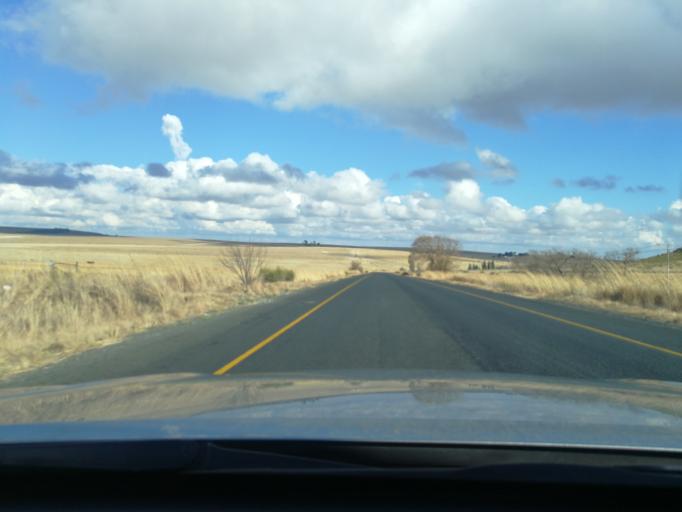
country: ZA
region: Orange Free State
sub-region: Thabo Mofutsanyana District Municipality
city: Reitz
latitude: -27.8993
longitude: 28.3958
